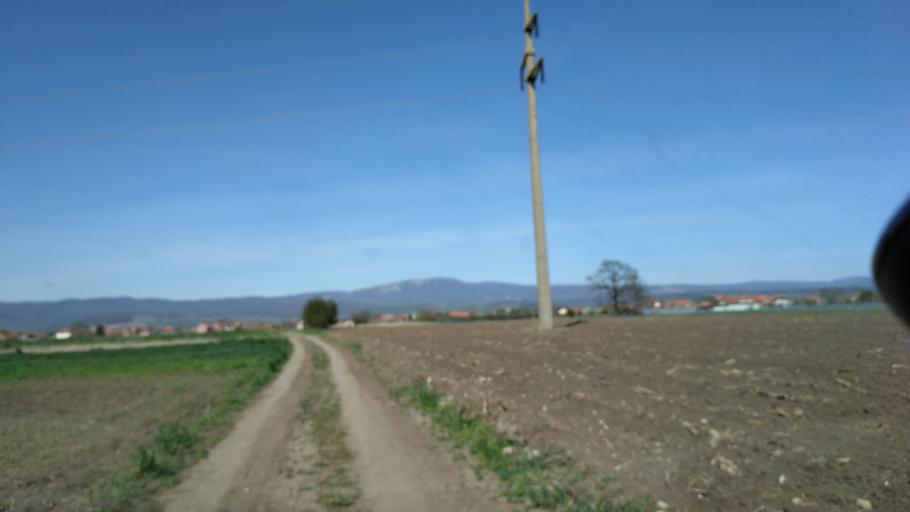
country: RS
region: Central Serbia
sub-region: Nisavski Okrug
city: Aleksinac
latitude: 43.4918
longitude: 21.6924
